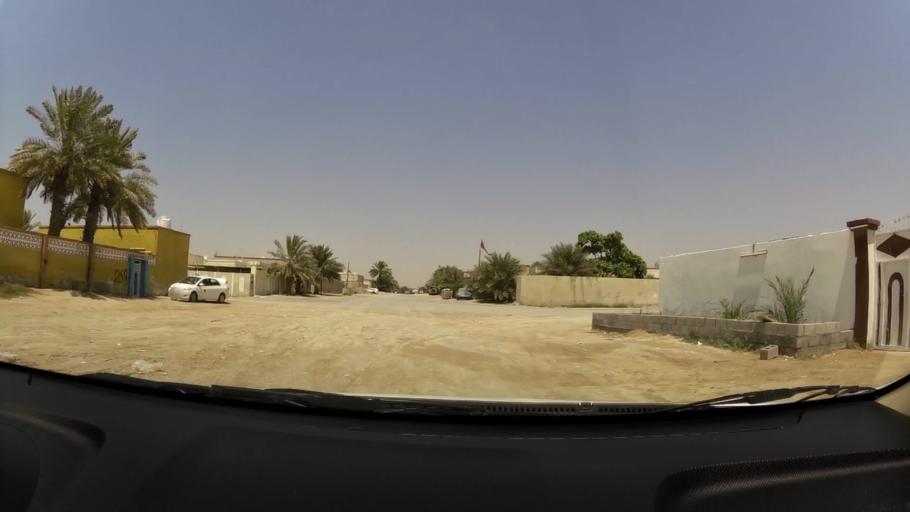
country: AE
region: Umm al Qaywayn
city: Umm al Qaywayn
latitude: 25.5056
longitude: 55.5741
